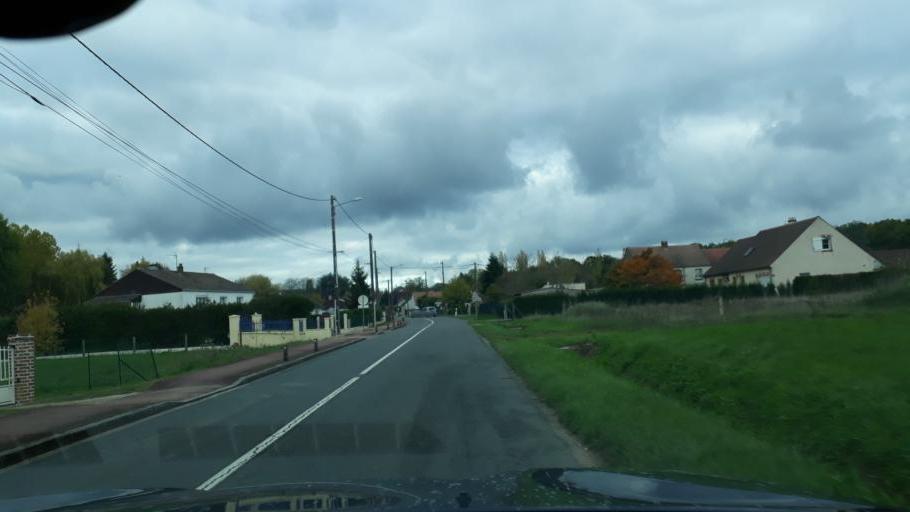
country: FR
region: Centre
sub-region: Departement du Loiret
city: Bray-en-Val
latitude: 47.8072
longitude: 2.3977
